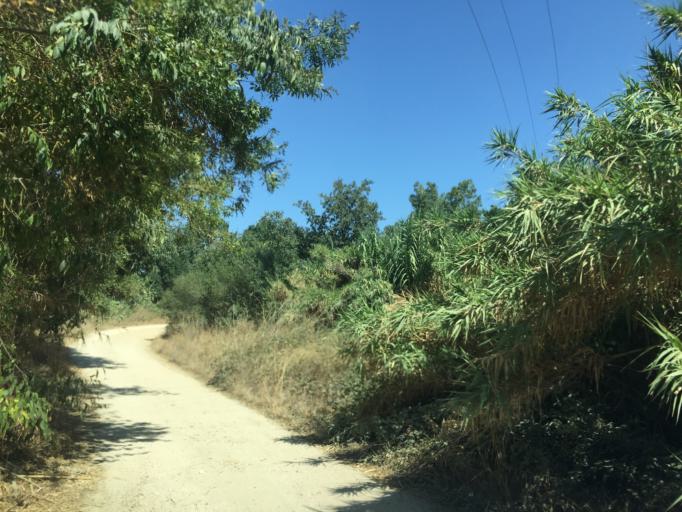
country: PT
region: Santarem
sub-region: Chamusca
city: Vila Nova da Barquinha
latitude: 39.4524
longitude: -8.4465
